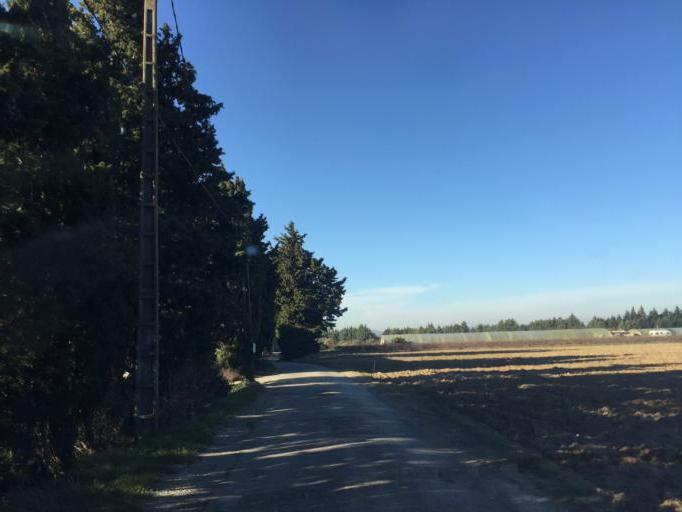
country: FR
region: Provence-Alpes-Cote d'Azur
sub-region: Departement du Vaucluse
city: Orange
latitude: 44.1536
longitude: 4.8208
